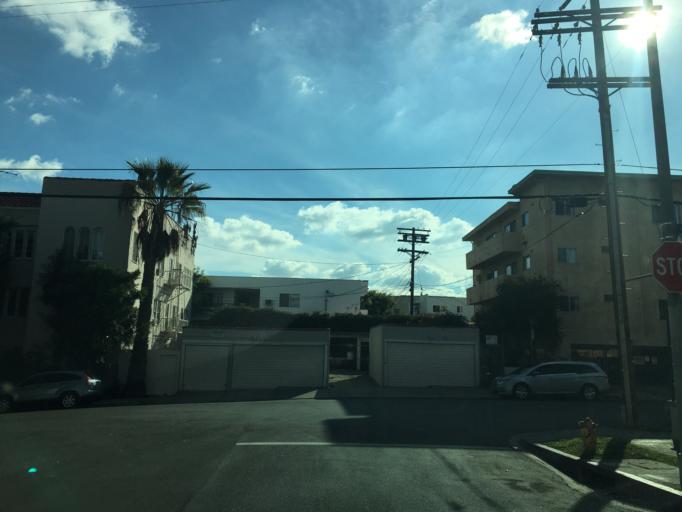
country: US
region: California
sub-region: Los Angeles County
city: Silver Lake
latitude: 34.0714
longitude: -118.2984
